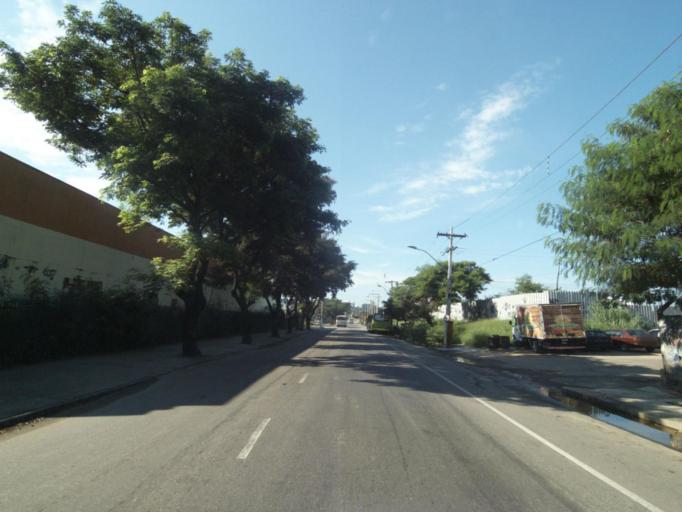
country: BR
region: Rio de Janeiro
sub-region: Niteroi
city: Niteroi
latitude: -22.8867
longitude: -43.1276
